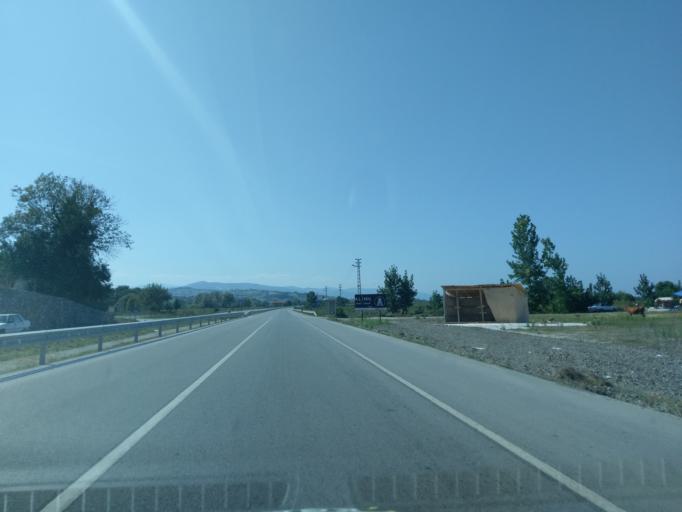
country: TR
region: Samsun
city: Alacam
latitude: 41.6084
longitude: 35.6714
